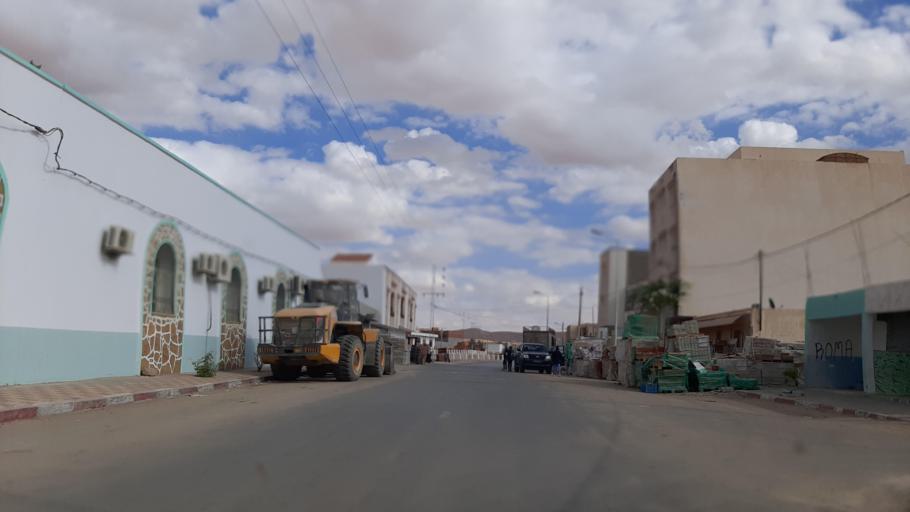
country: TN
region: Tataouine
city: Tataouine
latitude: 32.9201
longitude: 10.4649
